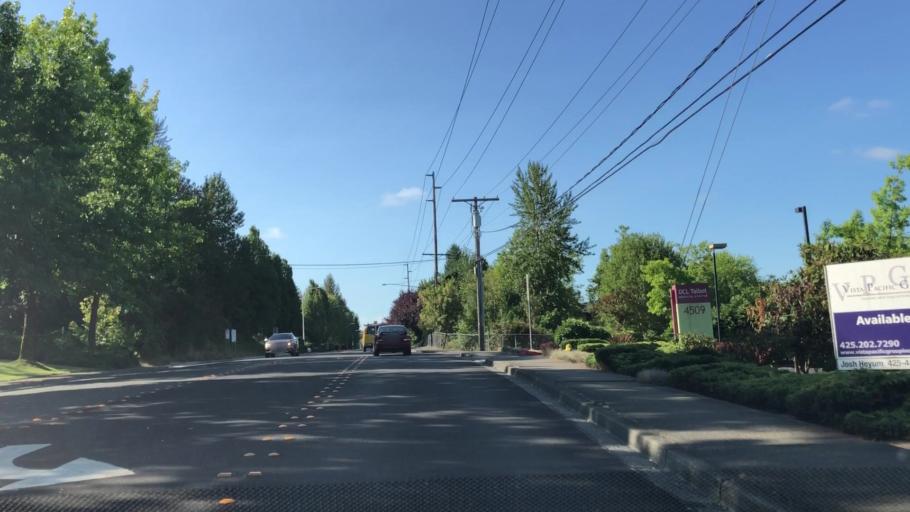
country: US
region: Washington
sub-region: King County
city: Renton
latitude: 47.4394
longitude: -122.2131
